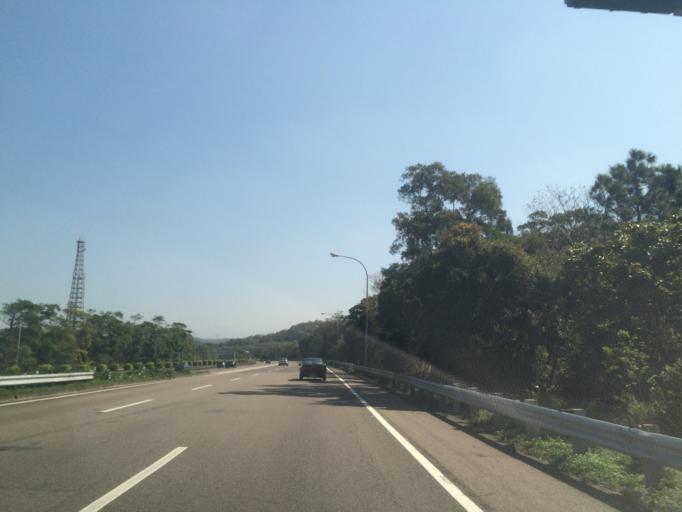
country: TW
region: Taiwan
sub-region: Hsinchu
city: Hsinchu
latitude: 24.7562
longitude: 120.9904
